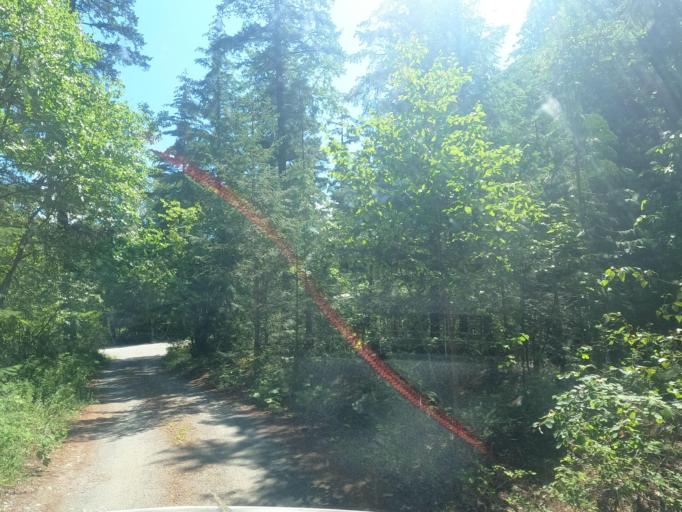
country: CA
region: British Columbia
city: Lillooet
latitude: 50.6132
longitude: -122.1059
